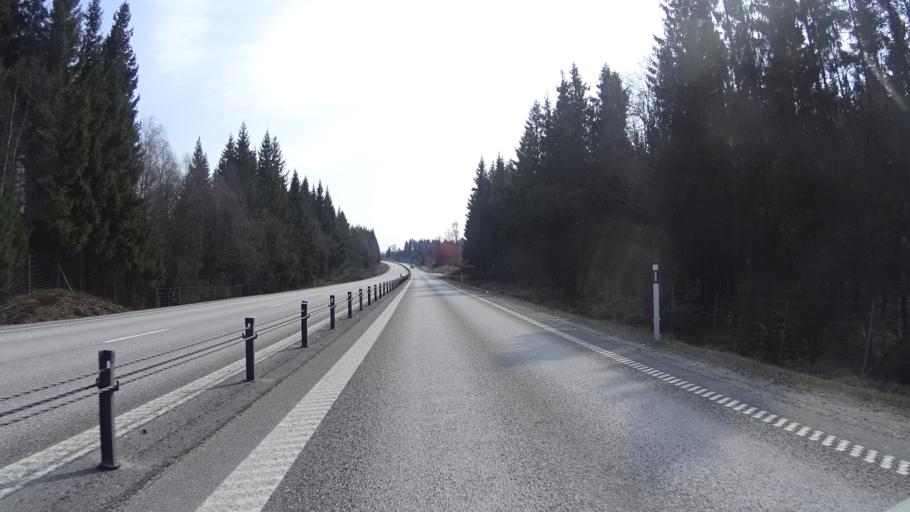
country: SE
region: Vaestra Goetaland
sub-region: Ulricehamns Kommun
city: Ulricehamn
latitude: 57.7846
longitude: 13.6467
